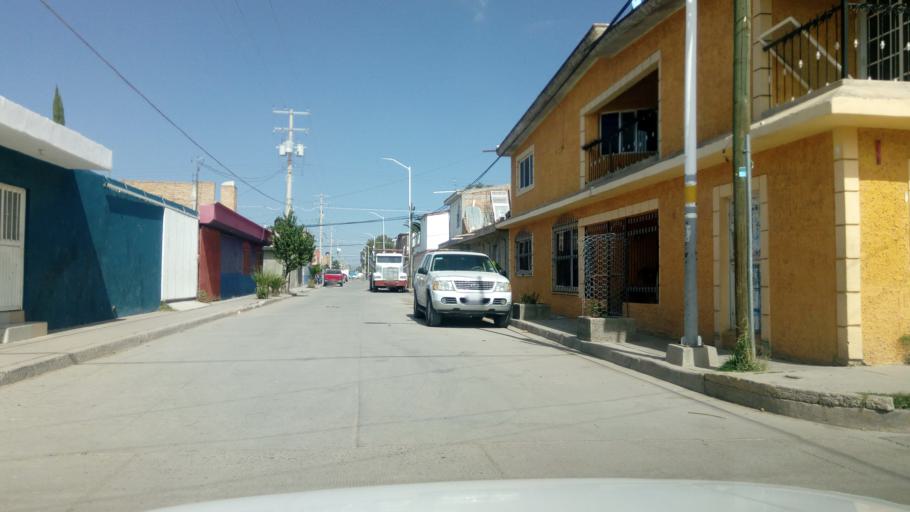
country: MX
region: Durango
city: Victoria de Durango
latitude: 23.9864
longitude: -104.6553
